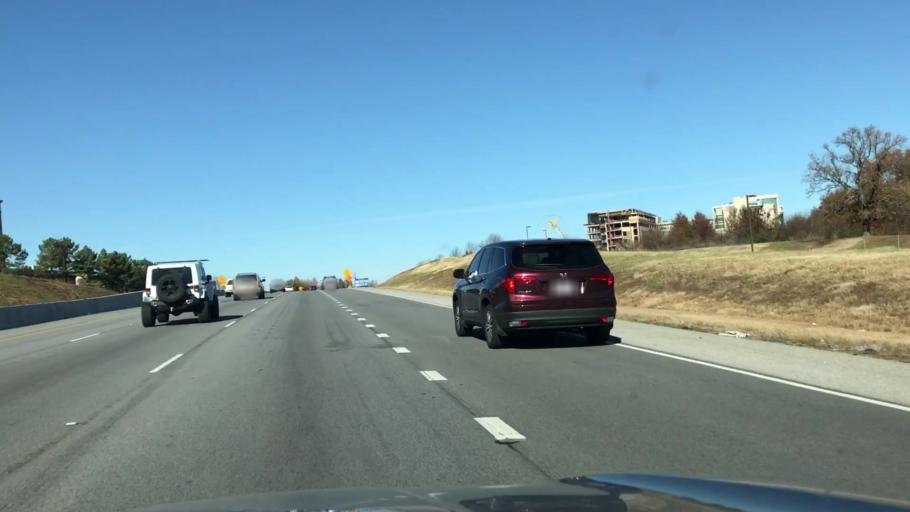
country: US
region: Arkansas
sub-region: Benton County
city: Cave Springs
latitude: 36.3043
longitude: -94.1826
